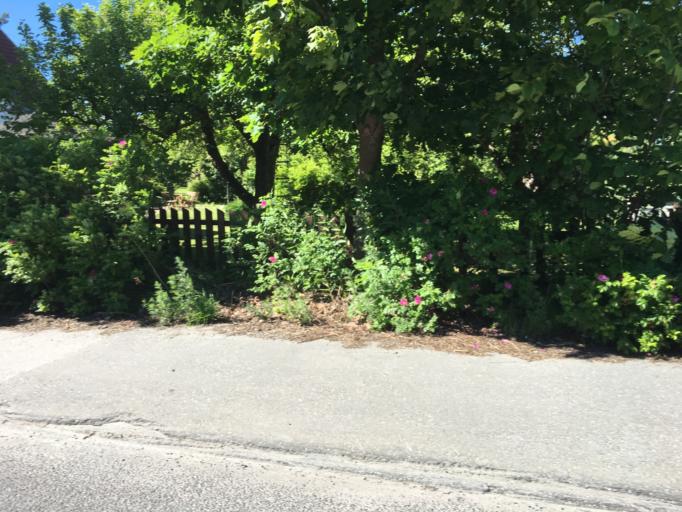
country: SE
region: Stockholm
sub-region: Sollentuna Kommun
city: Sollentuna
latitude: 59.4160
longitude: 17.9586
